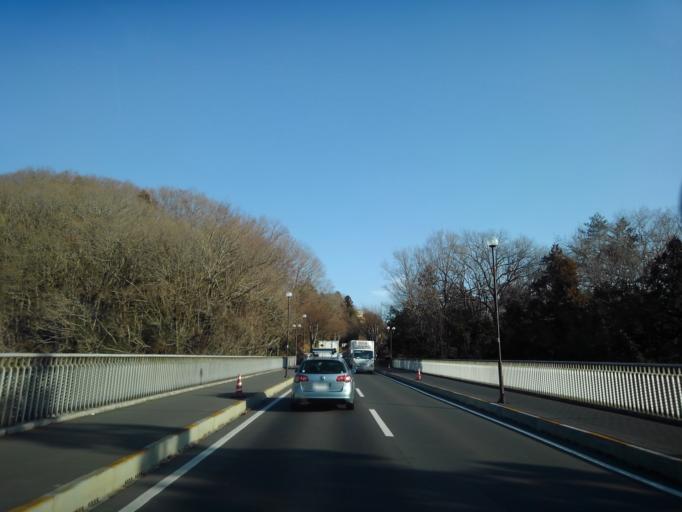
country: JP
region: Saitama
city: Hanno
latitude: 35.8386
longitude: 139.3088
